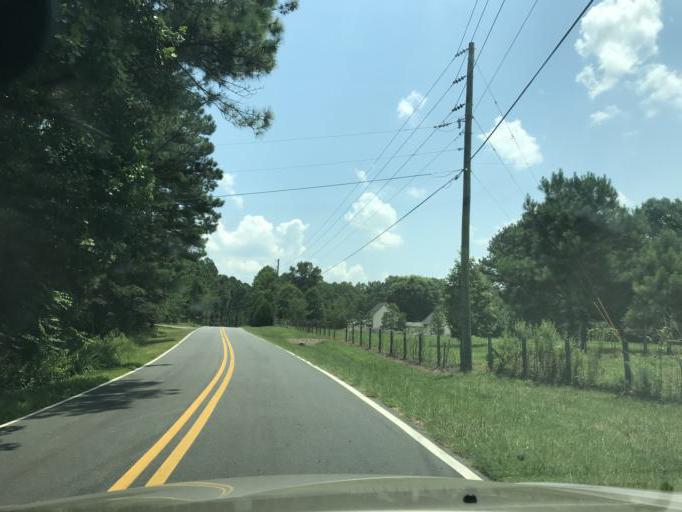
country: US
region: Georgia
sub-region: Forsyth County
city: Cumming
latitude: 34.3088
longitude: -84.1908
